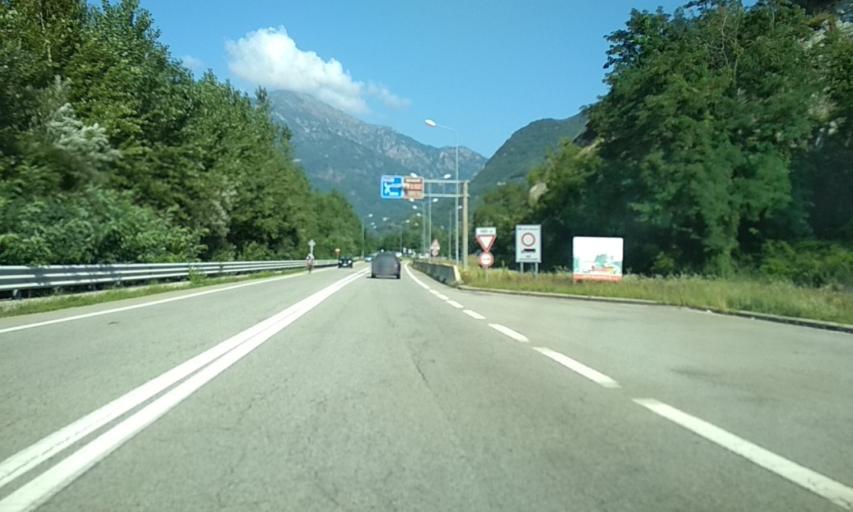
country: IT
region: Piedmont
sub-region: Provincia di Torino
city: Pont-Canavese
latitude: 45.4119
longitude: 7.6203
